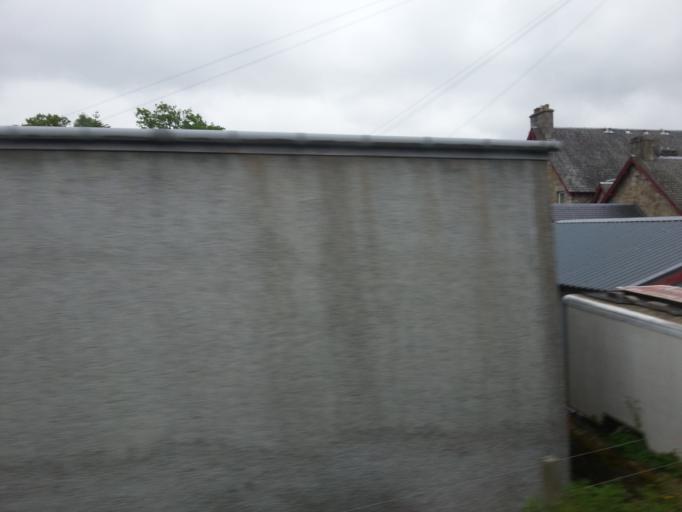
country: GB
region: Scotland
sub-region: Perth and Kinross
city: Pitlochry
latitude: 56.7017
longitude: -3.7316
